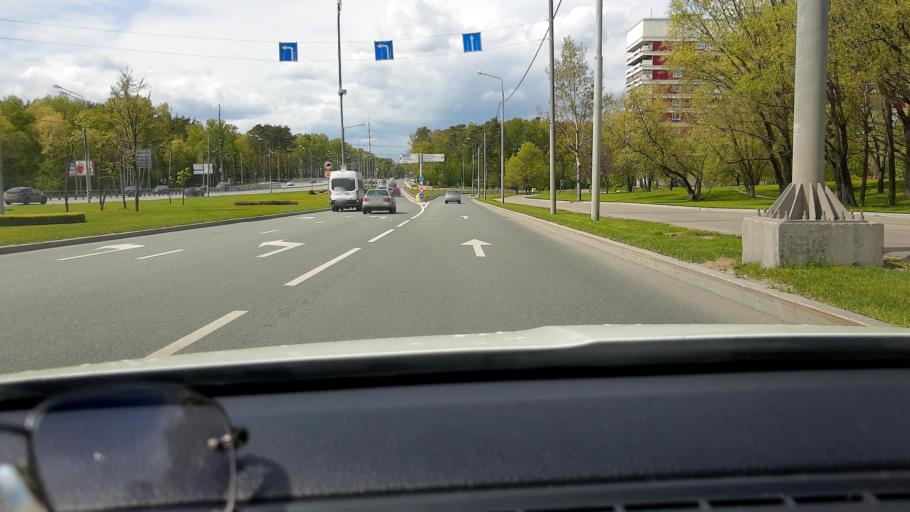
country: RU
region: Moskovskaya
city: Bol'shaya Setun'
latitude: 55.7571
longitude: 37.4002
